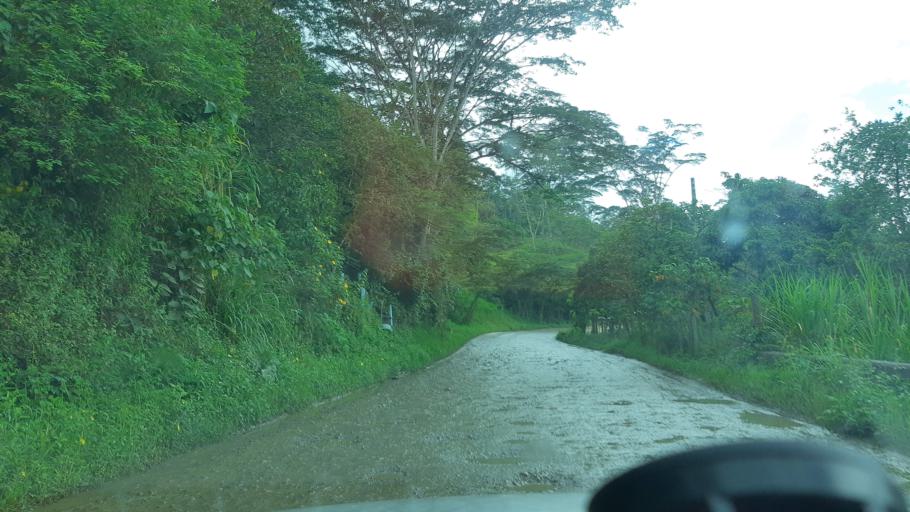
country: CO
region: Boyaca
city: Garagoa
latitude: 5.1209
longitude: -73.3621
